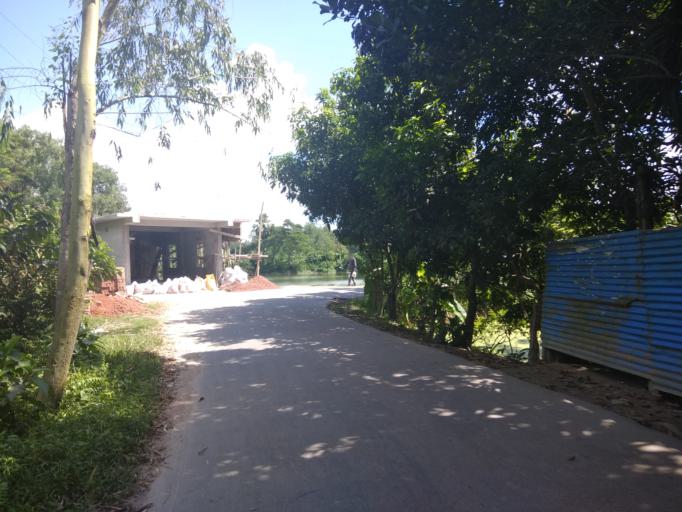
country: BD
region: Dhaka
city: Narayanganj
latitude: 23.4469
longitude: 90.4796
